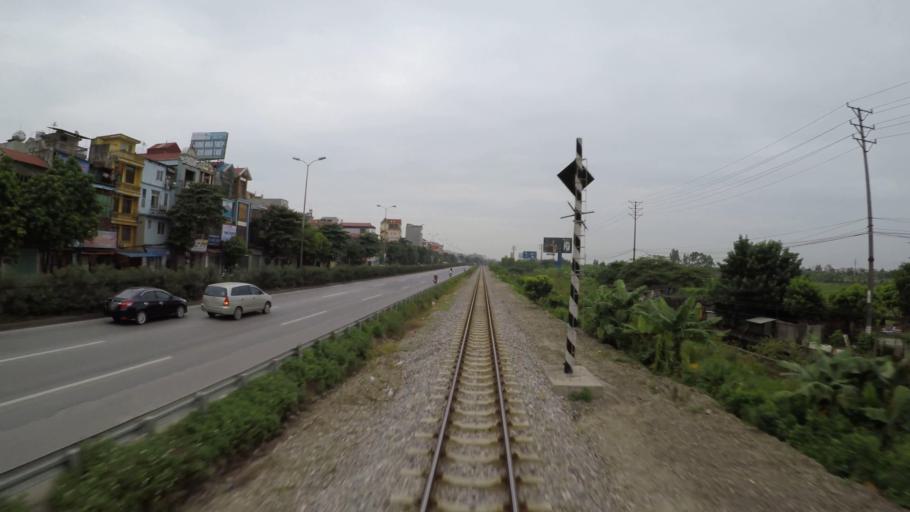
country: VN
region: Hung Yen
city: Nhu Quynh
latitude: 20.9878
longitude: 105.9765
